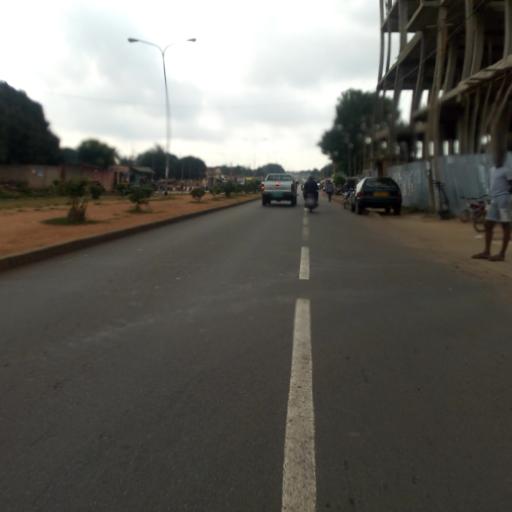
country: TG
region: Maritime
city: Lome
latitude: 6.1898
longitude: 1.2517
